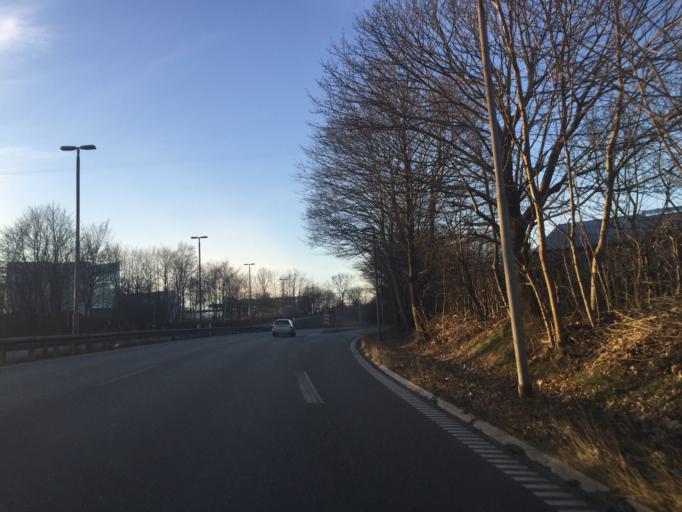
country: DK
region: Capital Region
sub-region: Lyngby-Tarbaek Kommune
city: Kongens Lyngby
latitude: 55.7805
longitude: 12.4866
